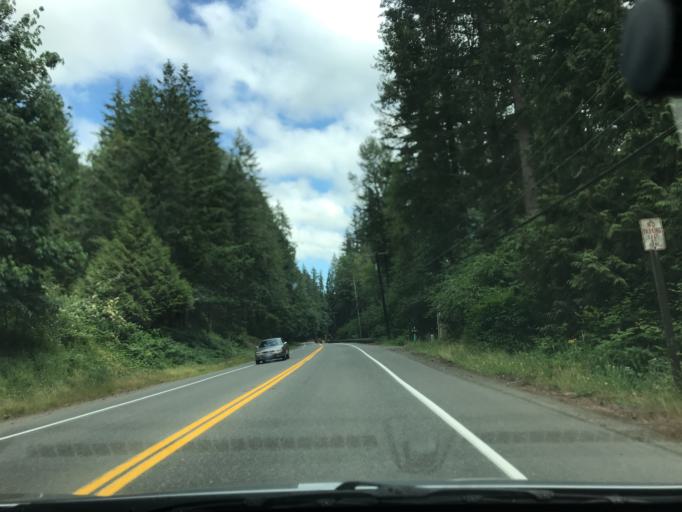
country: US
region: Washington
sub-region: King County
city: Lake Morton-Berrydale
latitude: 47.3091
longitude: -122.0906
